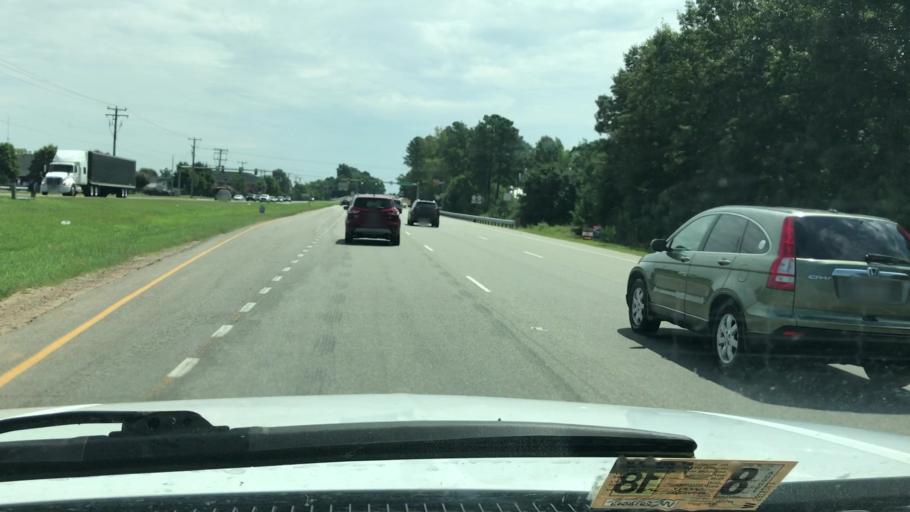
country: US
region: Virginia
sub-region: Chesterfield County
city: Brandermill
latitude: 37.5086
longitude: -77.6795
